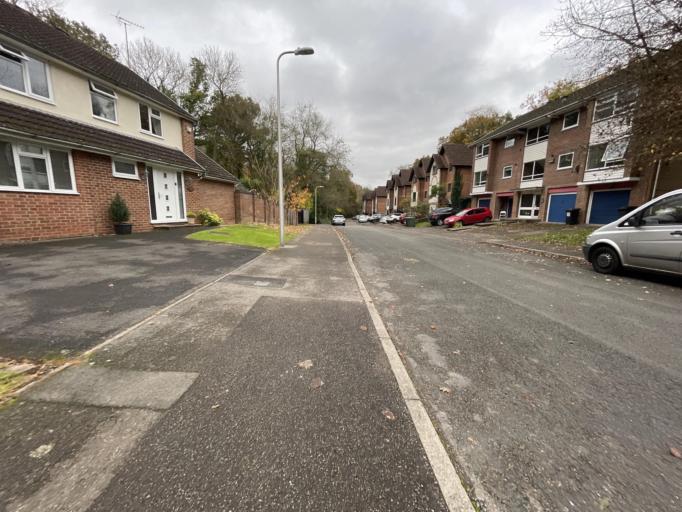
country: GB
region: England
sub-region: West Berkshire
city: Calcot
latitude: 51.4477
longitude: -1.0534
